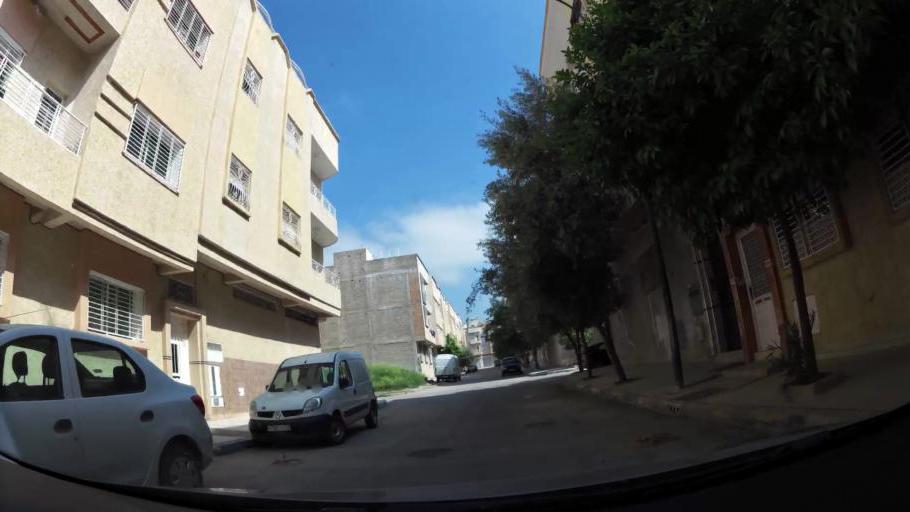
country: MA
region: Fes-Boulemane
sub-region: Fes
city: Fes
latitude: 34.0557
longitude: -5.0266
